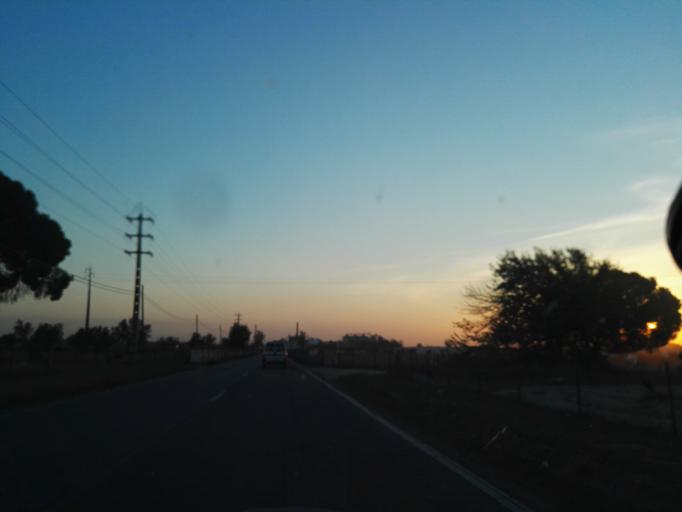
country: PT
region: Santarem
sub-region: Coruche
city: Coruche
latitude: 38.9516
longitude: -8.4957
